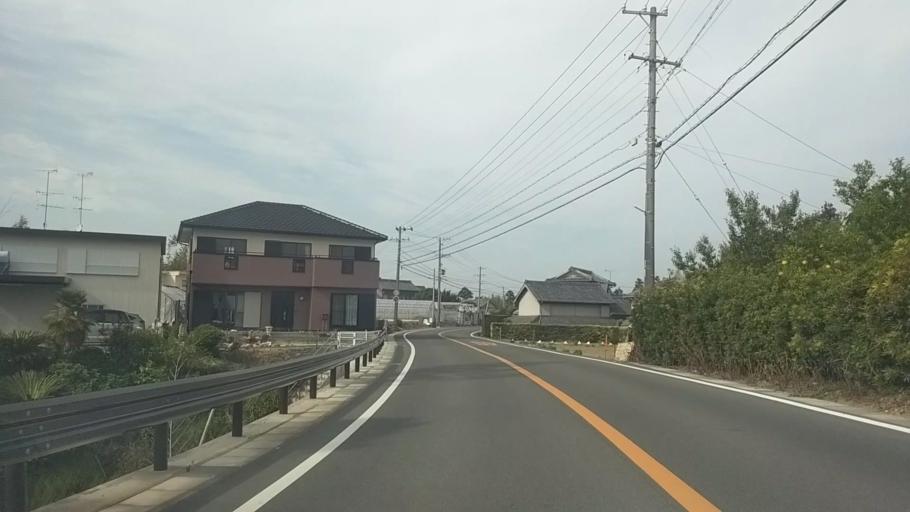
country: JP
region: Shizuoka
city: Hamamatsu
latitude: 34.7122
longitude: 137.6426
